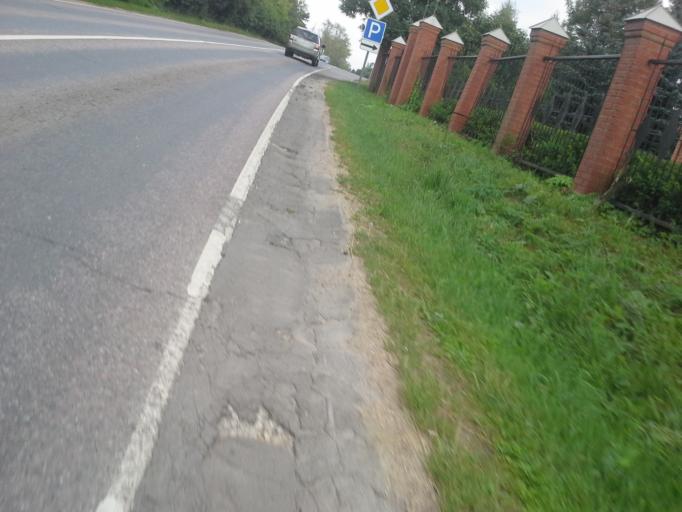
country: RU
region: Moskovskaya
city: Istra
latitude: 55.9315
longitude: 36.9295
